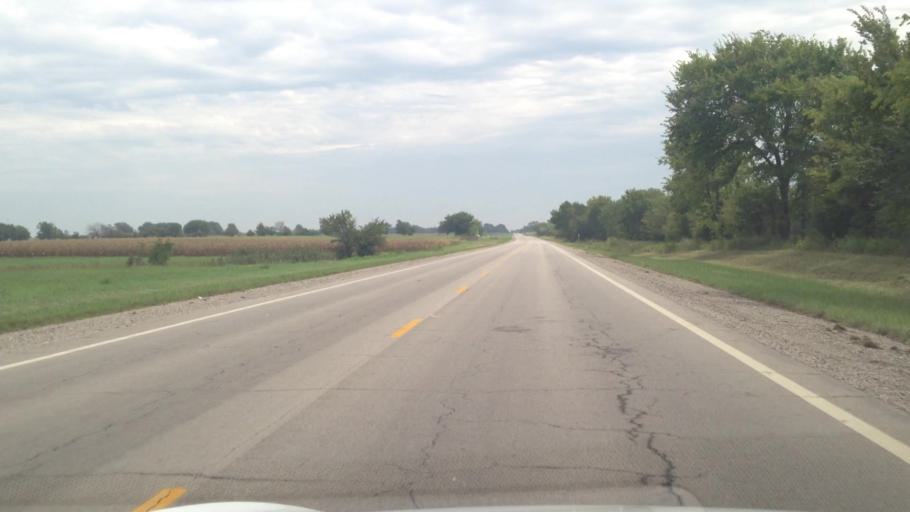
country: US
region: Kansas
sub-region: Crawford County
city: Girard
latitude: 37.5142
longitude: -94.8828
